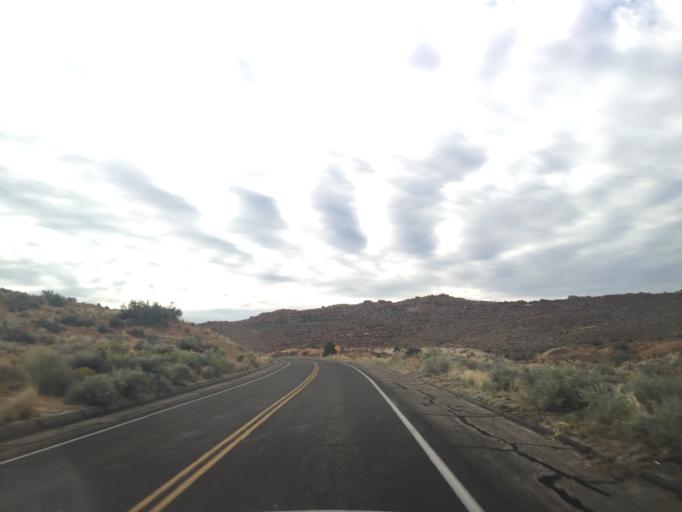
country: US
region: Utah
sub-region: Grand County
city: Moab
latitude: 38.7301
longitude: -109.5422
